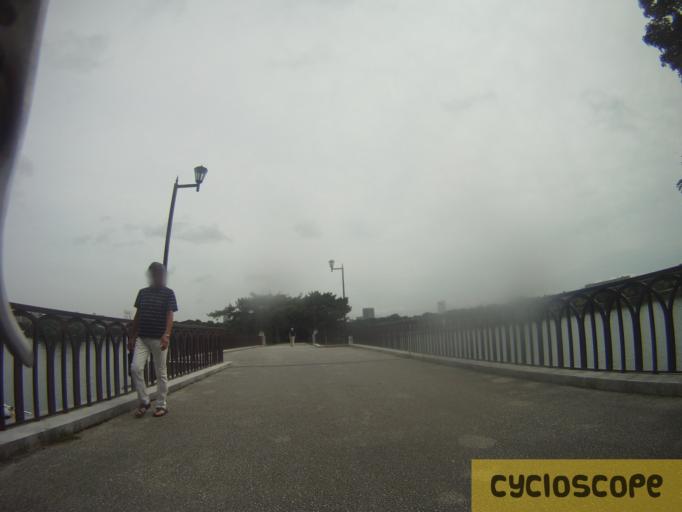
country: JP
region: Fukuoka
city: Fukuoka-shi
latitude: 33.5860
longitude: 130.3763
